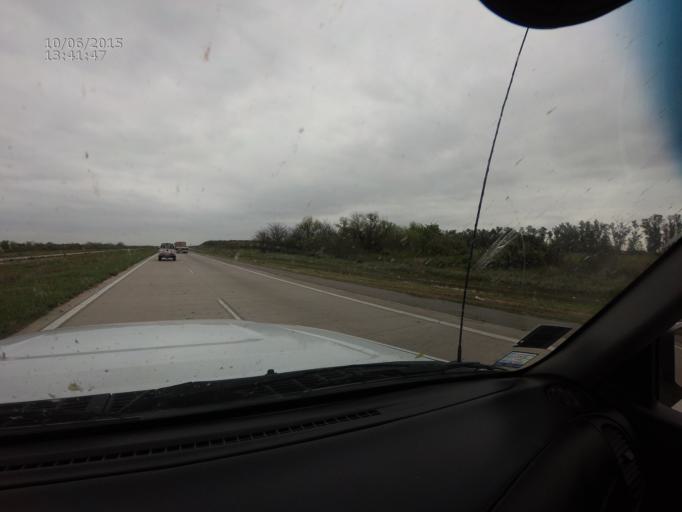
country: AR
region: Cordoba
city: Bell Ville
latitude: -32.5915
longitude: -62.5070
